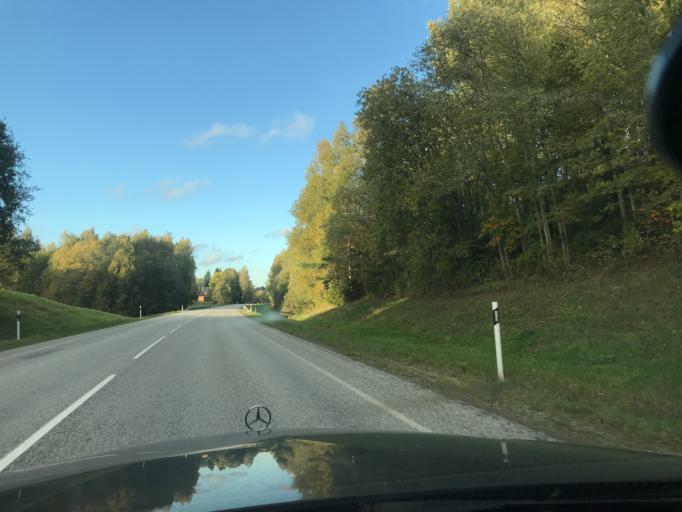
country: RU
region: Pskov
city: Pechory
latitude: 57.6788
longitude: 27.3262
